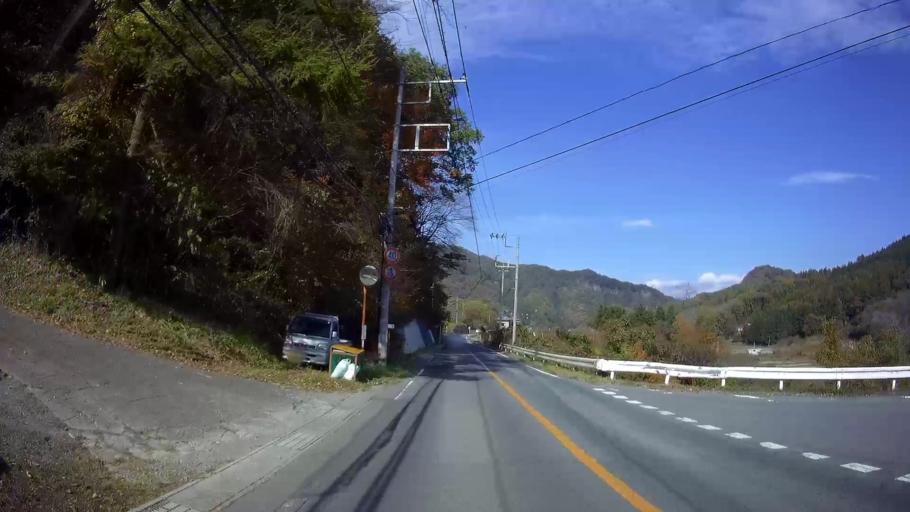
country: JP
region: Gunma
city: Nakanojomachi
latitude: 36.5037
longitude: 138.7769
